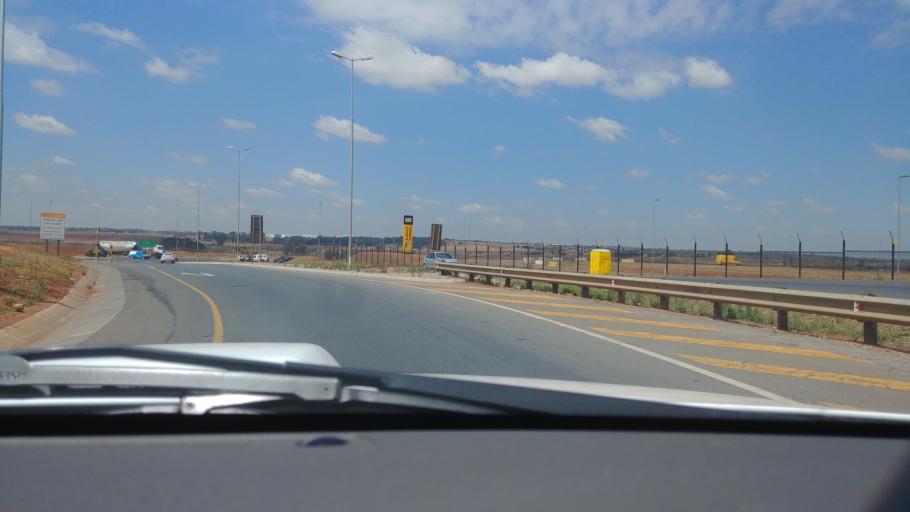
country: ZA
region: Gauteng
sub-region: Ekurhuleni Metropolitan Municipality
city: Tembisa
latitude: -26.0302
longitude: 28.2635
